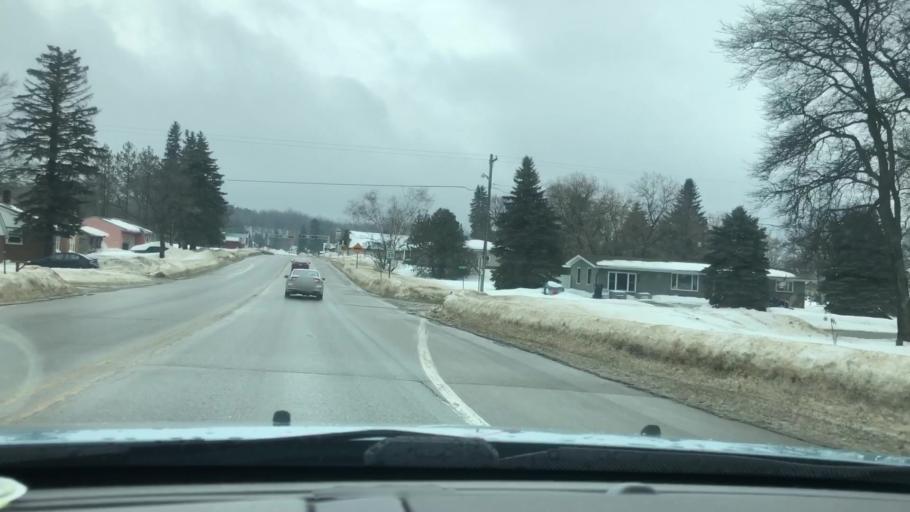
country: US
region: Michigan
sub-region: Otsego County
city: Gaylord
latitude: 45.0655
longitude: -84.8573
